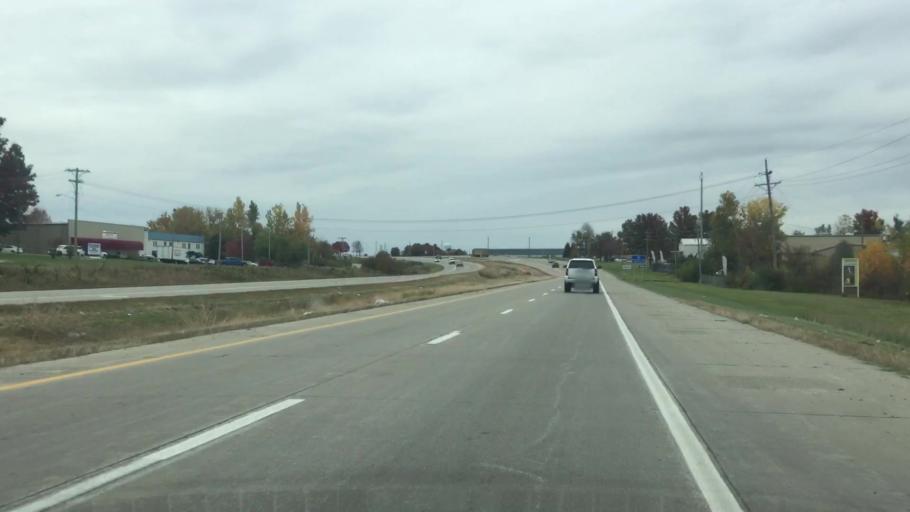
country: US
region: Missouri
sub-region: Jackson County
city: Lees Summit
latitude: 38.8890
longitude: -94.3732
